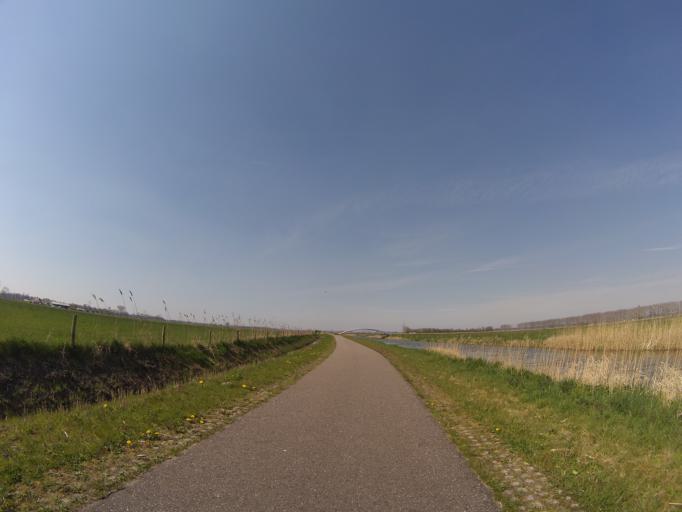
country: NL
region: Gelderland
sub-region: Gemeente Wageningen
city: Wageningen
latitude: 51.9788
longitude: 5.6187
